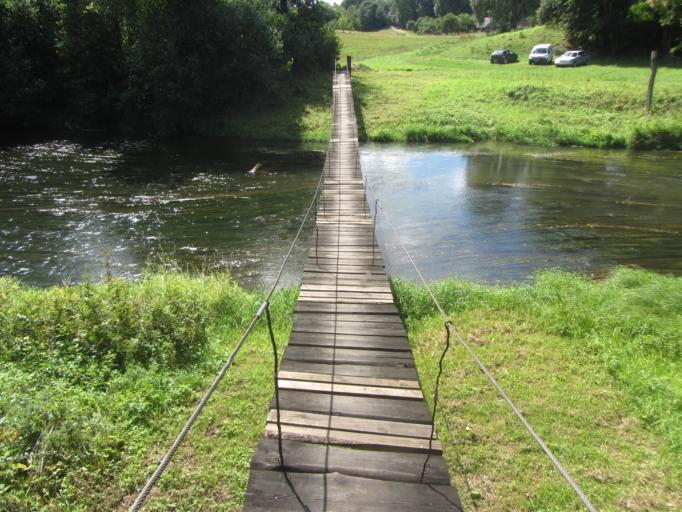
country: LT
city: Jieznas
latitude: 54.5961
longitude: 24.0990
